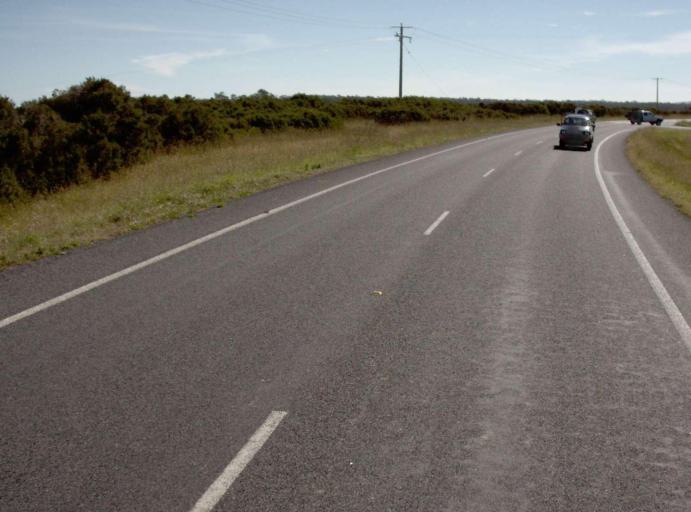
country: AU
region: Victoria
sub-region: Latrobe
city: Traralgon
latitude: -38.6346
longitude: 146.5842
